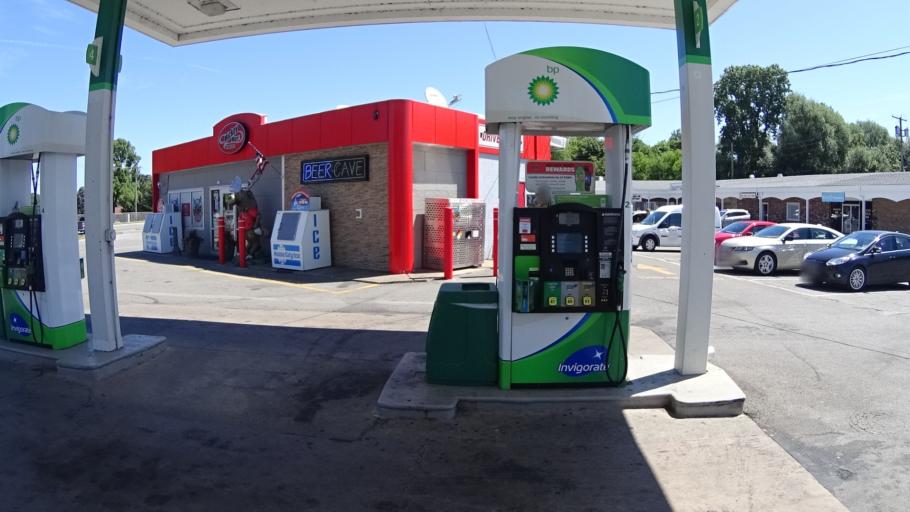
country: US
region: Ohio
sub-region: Erie County
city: Sandusky
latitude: 41.4152
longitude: -82.6873
